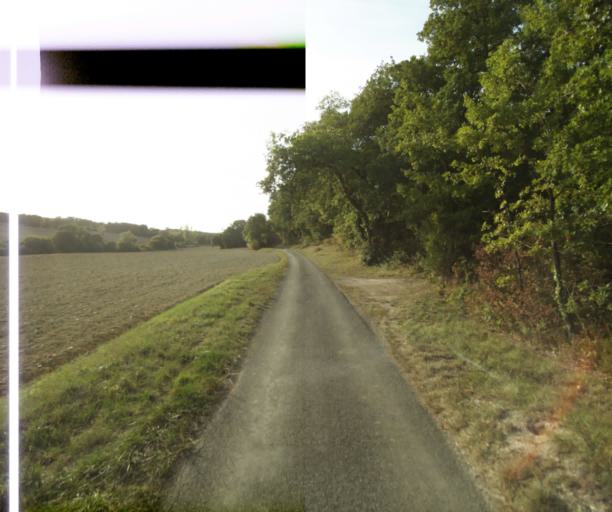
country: FR
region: Midi-Pyrenees
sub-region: Departement du Gers
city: Gondrin
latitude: 43.9018
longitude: 0.2692
